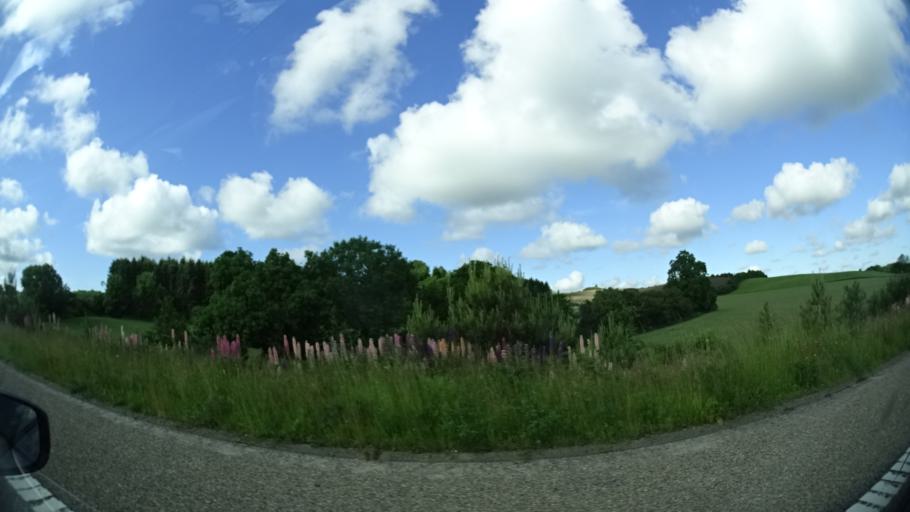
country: DK
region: Central Jutland
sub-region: Syddjurs Kommune
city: Ronde
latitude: 56.3094
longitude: 10.5006
